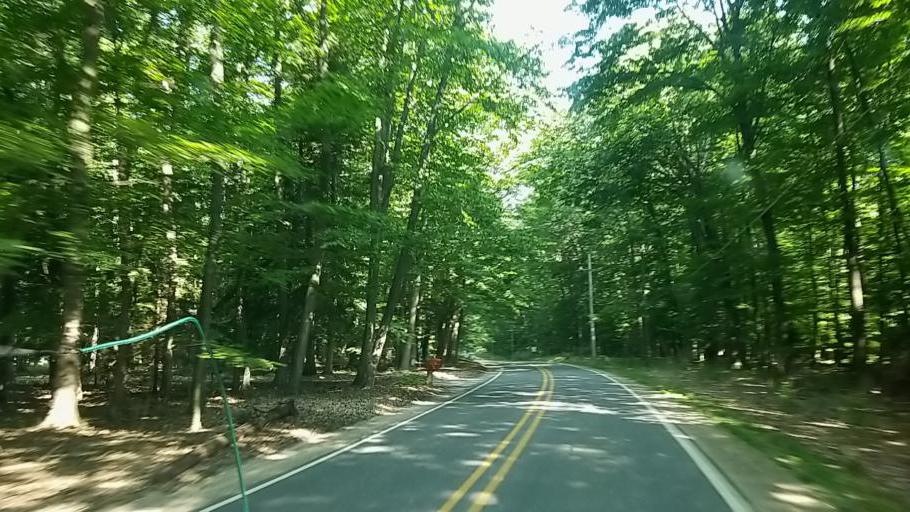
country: US
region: Michigan
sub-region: Muskegon County
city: Whitehall
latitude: 43.3231
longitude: -86.3961
